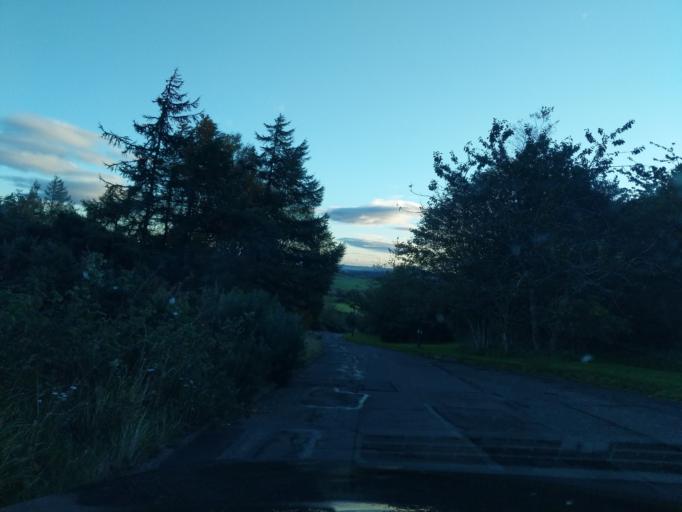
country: GB
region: Scotland
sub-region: Midlothian
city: Loanhead
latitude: 55.8893
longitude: -3.2070
